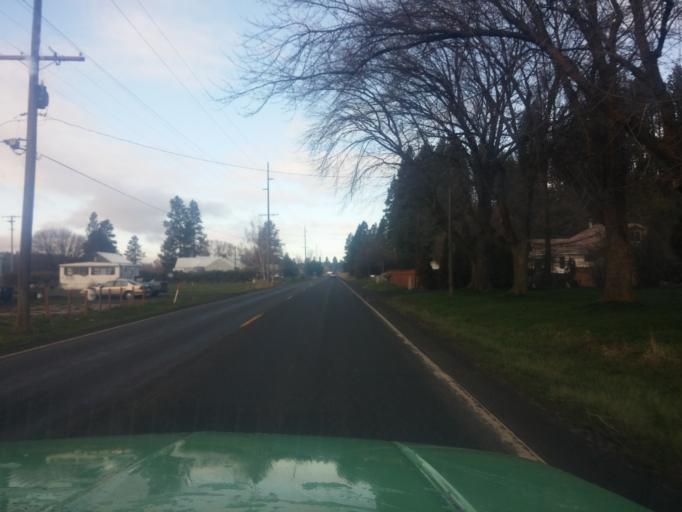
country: US
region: Idaho
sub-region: Latah County
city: Moscow
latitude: 46.9300
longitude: -116.9207
